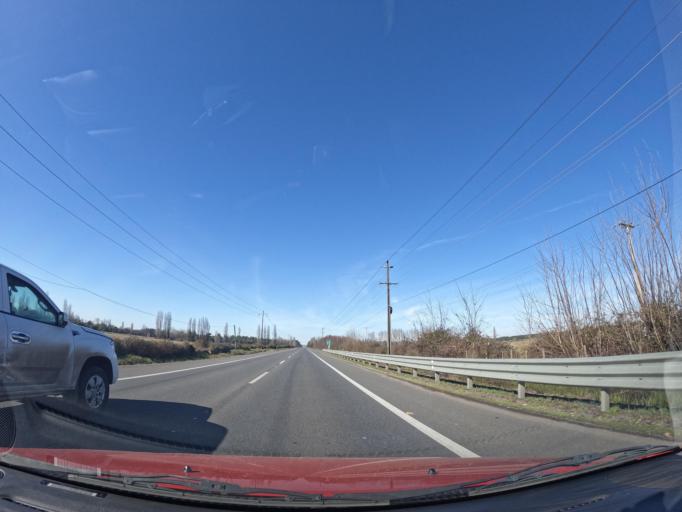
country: CL
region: Biobio
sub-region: Provincia de Biobio
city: Cabrero
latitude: -37.0571
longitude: -72.3455
